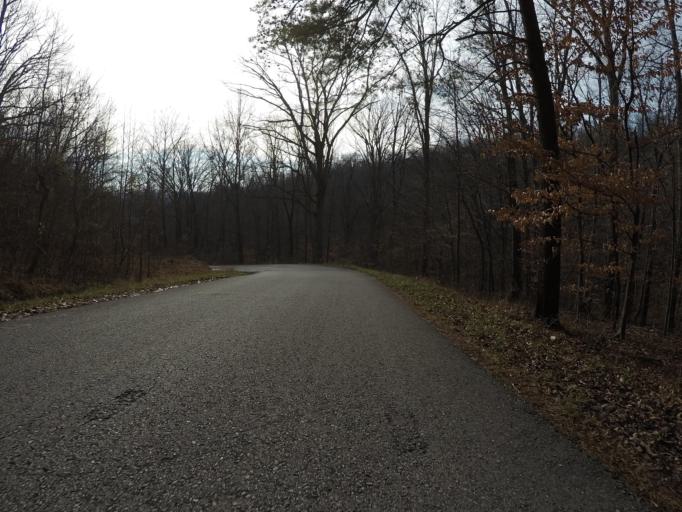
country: US
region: West Virginia
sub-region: Cabell County
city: Pea Ridge
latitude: 38.4305
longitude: -82.3385
